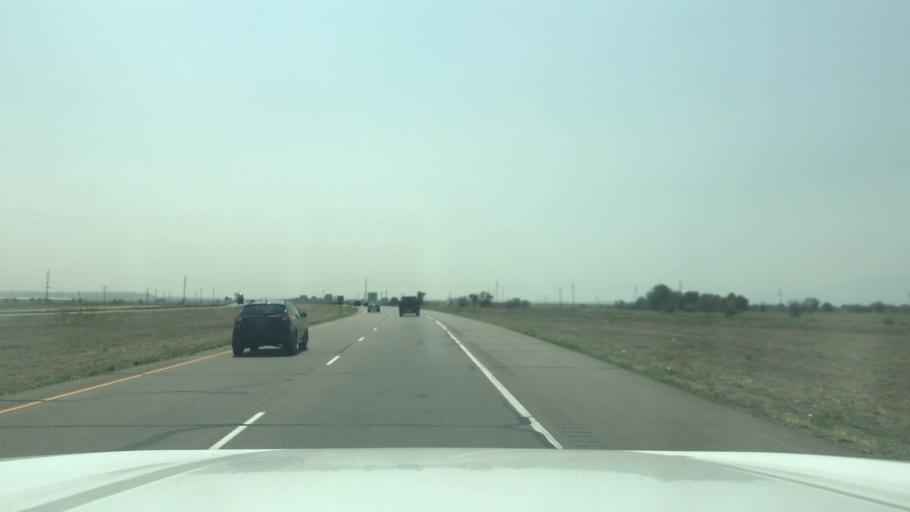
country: US
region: Colorado
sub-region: Pueblo County
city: Pueblo
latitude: 38.1993
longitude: -104.6321
